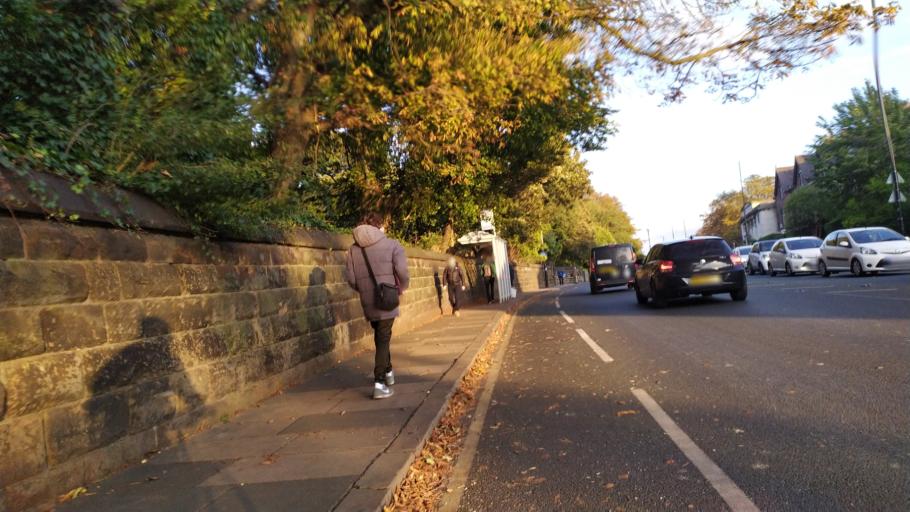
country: GB
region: England
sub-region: City and Borough of Leeds
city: Leeds
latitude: 53.8176
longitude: -1.5724
